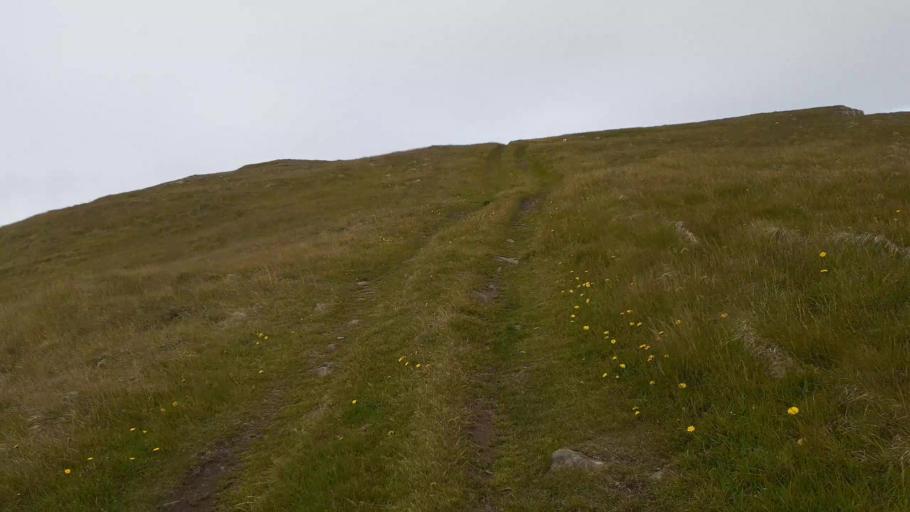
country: IS
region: Northeast
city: Dalvik
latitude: 66.5338
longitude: -17.9830
